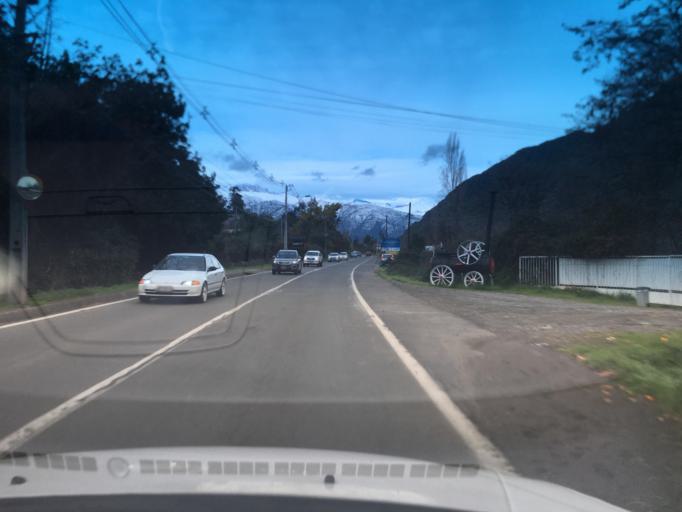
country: CL
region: Santiago Metropolitan
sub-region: Provincia de Cordillera
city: Puente Alto
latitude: -33.5766
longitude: -70.4416
